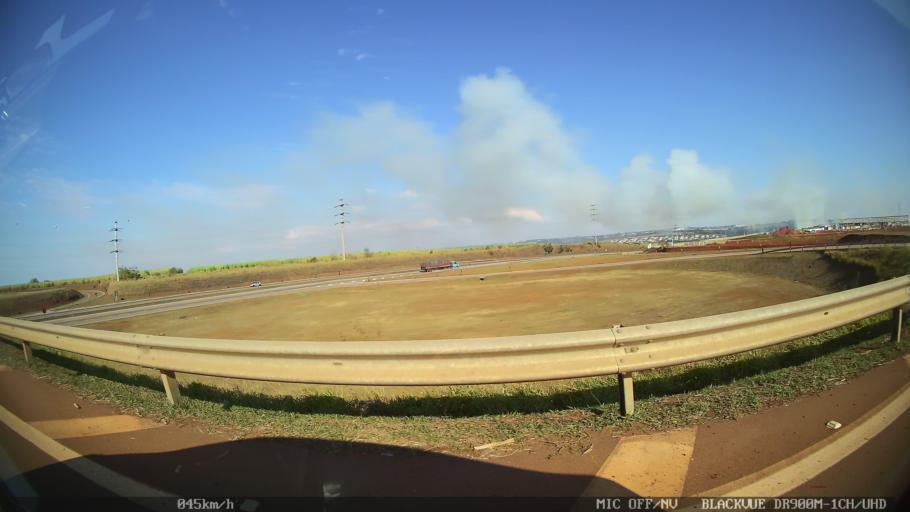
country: BR
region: Sao Paulo
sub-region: Piracicaba
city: Piracicaba
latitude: -22.6813
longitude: -47.5960
